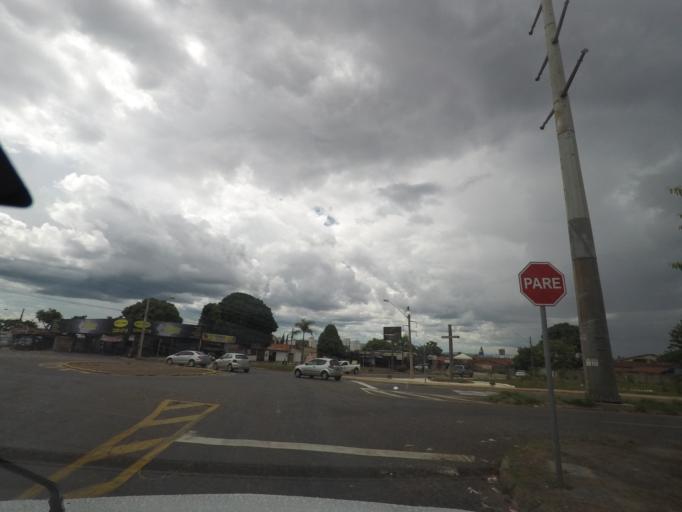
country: BR
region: Goias
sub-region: Goiania
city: Goiania
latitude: -16.7375
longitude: -49.3262
